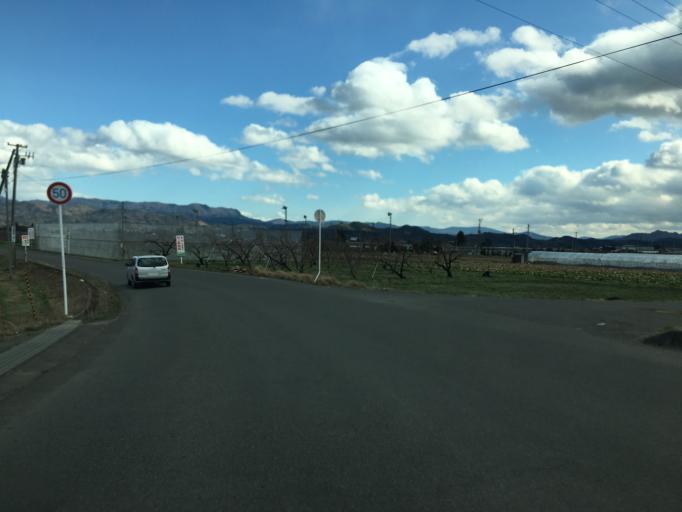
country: JP
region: Fukushima
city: Yanagawamachi-saiwaicho
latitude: 37.8598
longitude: 140.5707
